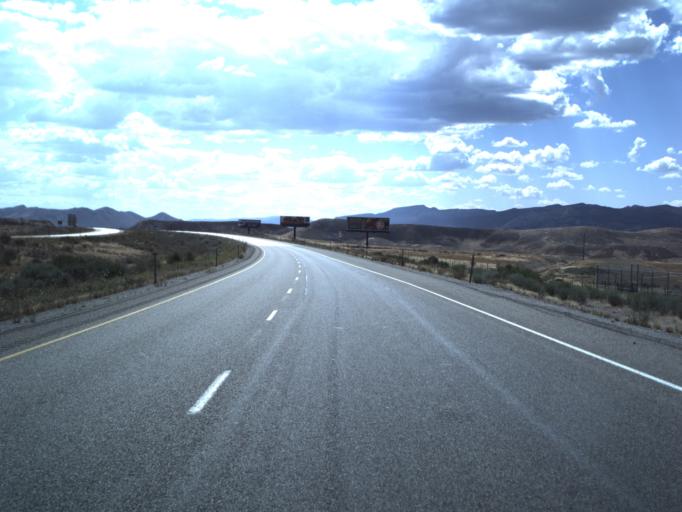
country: US
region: Utah
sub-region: Sevier County
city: Salina
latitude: 38.9315
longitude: -111.8654
